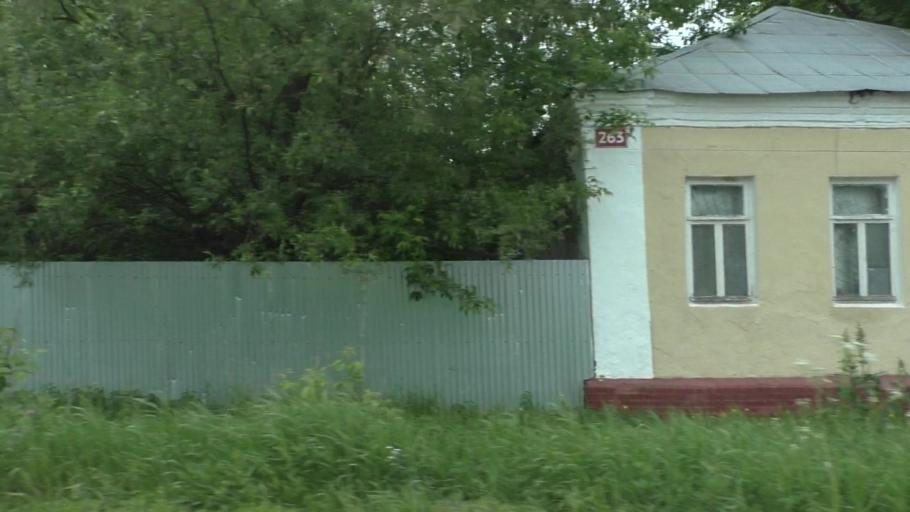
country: RU
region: Moskovskaya
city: Imeni Tsyurupy
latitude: 55.5057
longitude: 38.7737
